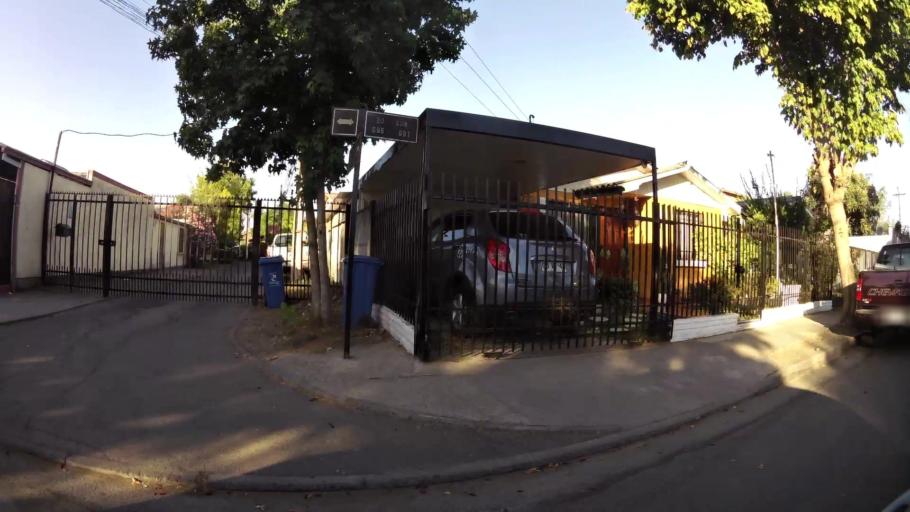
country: CL
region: Maule
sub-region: Provincia de Talca
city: Talca
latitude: -35.4455
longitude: -71.6724
